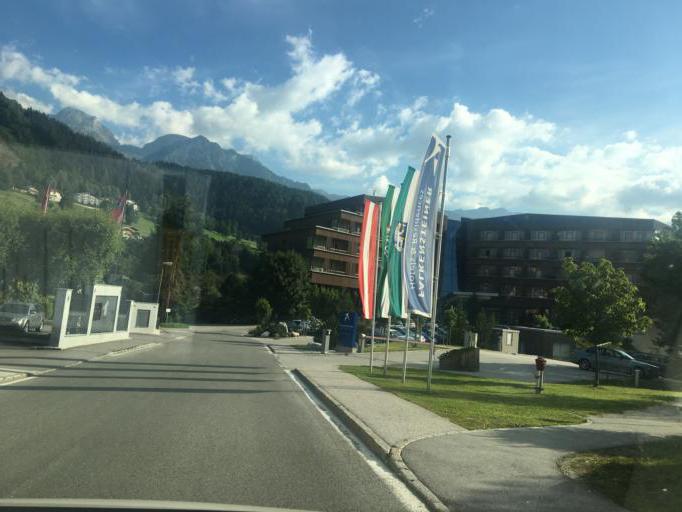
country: AT
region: Styria
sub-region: Politischer Bezirk Liezen
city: Schladming
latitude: 47.3960
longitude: 13.6951
